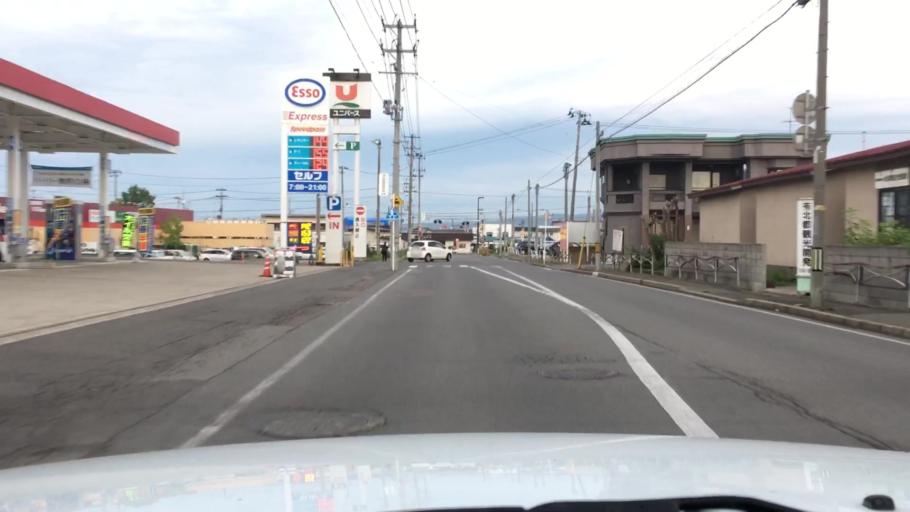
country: JP
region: Aomori
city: Hirosaki
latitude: 40.5912
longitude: 140.4864
